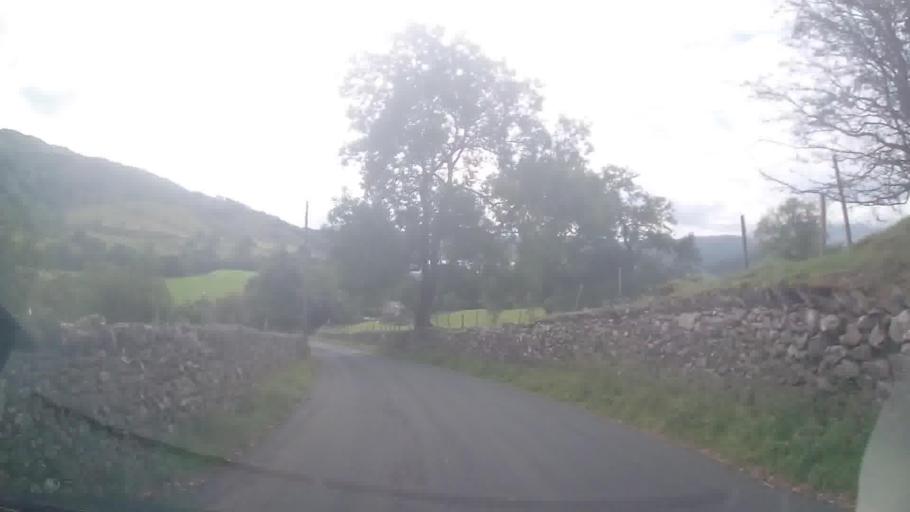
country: GB
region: England
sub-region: Cumbria
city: Ambleside
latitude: 54.4378
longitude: -2.9513
